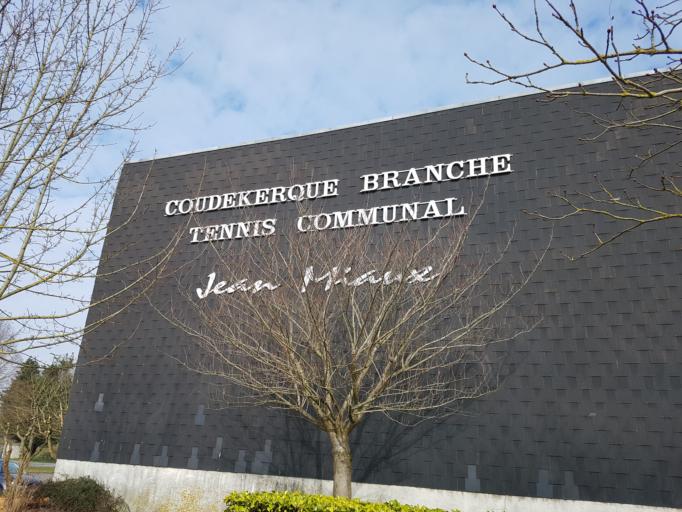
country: FR
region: Nord-Pas-de-Calais
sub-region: Departement du Nord
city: Coudekerque-Branche
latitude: 51.0133
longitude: 2.3854
